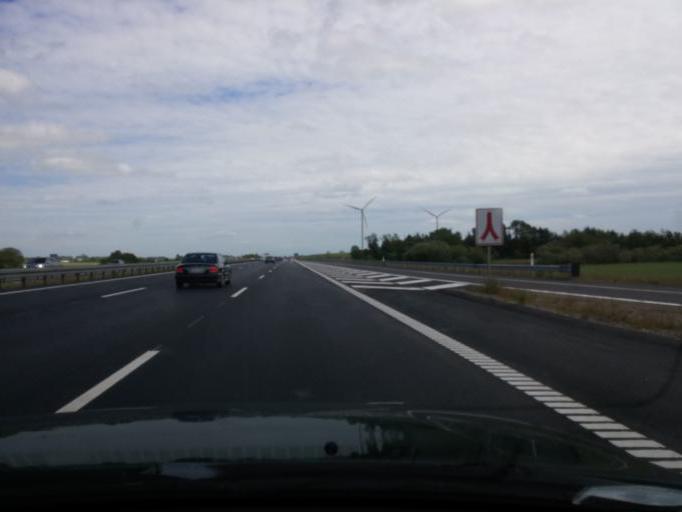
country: DK
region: South Denmark
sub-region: Middelfart Kommune
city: Norre Aby
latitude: 55.4926
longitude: 9.8187
